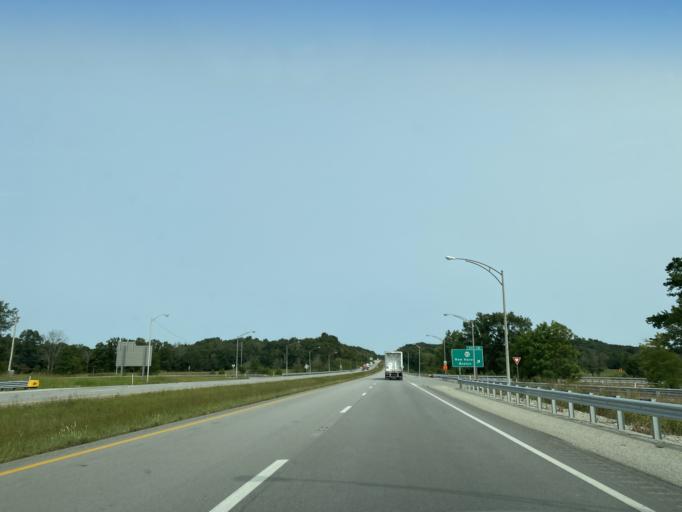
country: US
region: Kentucky
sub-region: Bullitt County
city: Lebanon Junction
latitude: 37.7494
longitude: -85.6720
